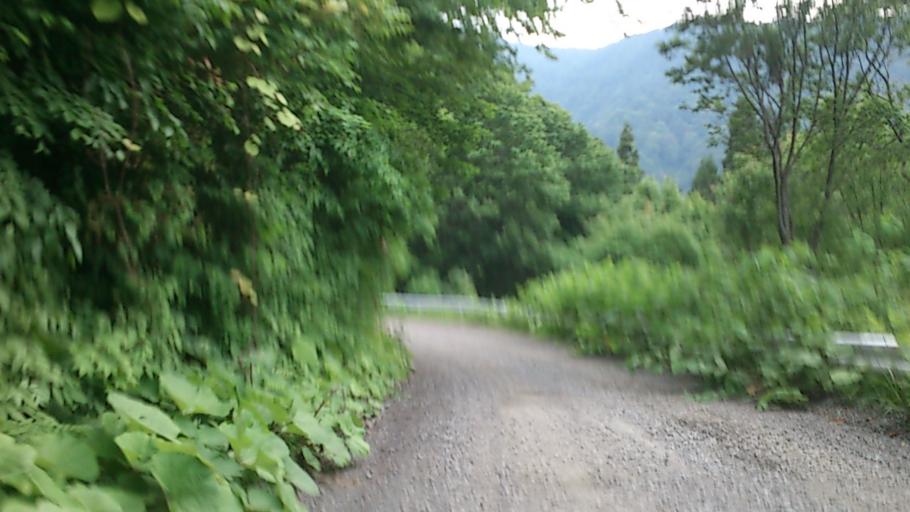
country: JP
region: Aomori
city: Hirosaki
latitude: 40.5541
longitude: 140.1793
